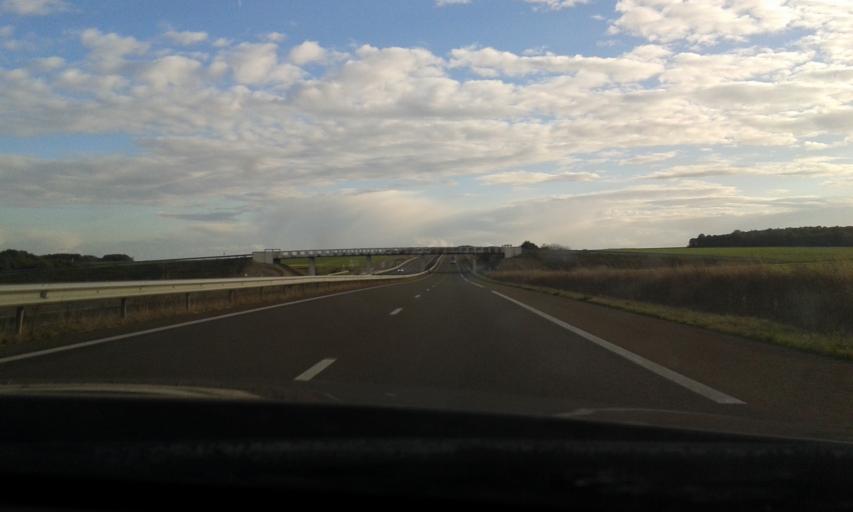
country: FR
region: Centre
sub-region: Departement d'Eure-et-Loir
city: Villemeux-sur-Eure
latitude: 48.6328
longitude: 1.4113
